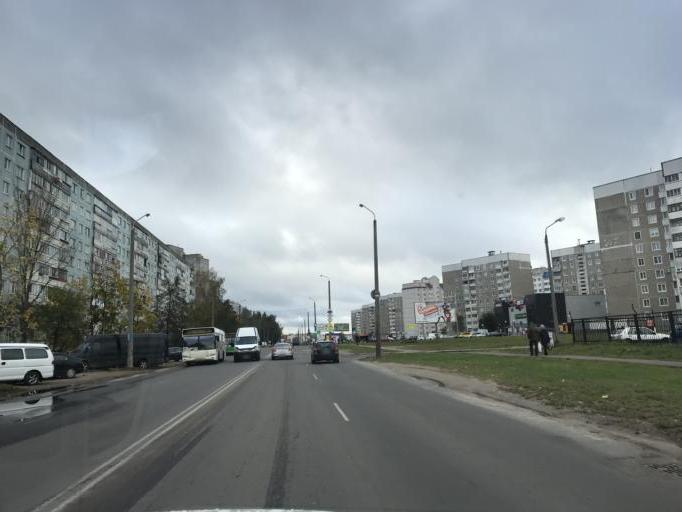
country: BY
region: Mogilev
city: Mahilyow
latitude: 53.8782
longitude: 30.3683
